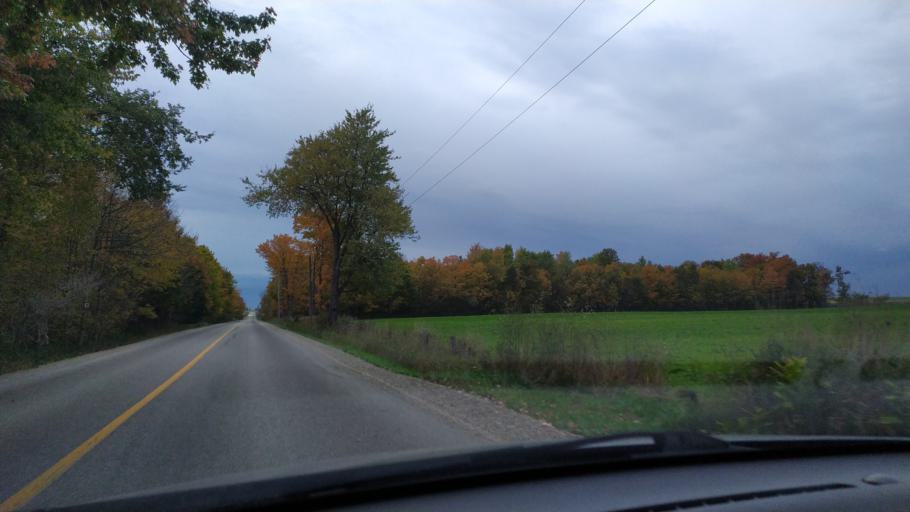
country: CA
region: Ontario
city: Waterloo
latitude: 43.5124
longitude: -80.7402
